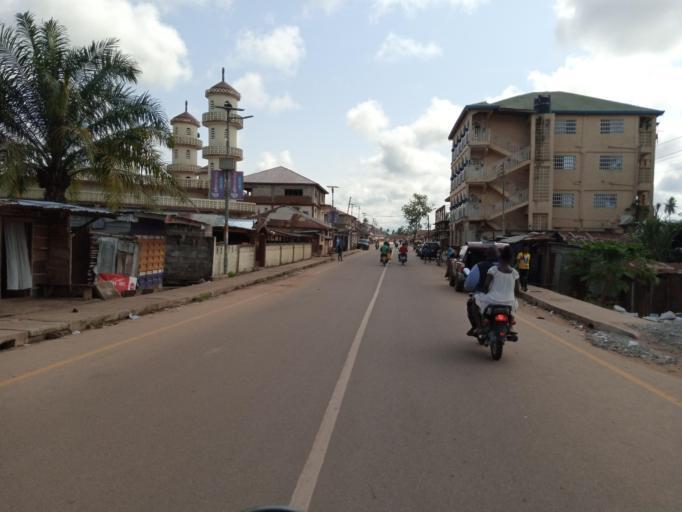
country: SL
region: Southern Province
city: Bo
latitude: 7.9675
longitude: -11.7396
